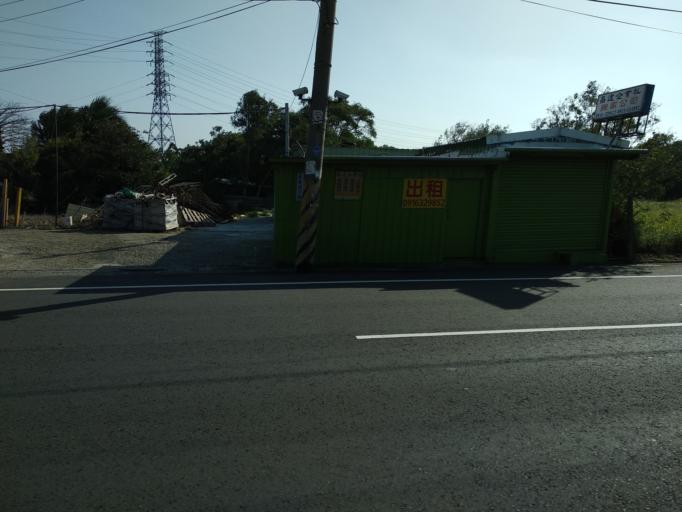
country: TW
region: Taiwan
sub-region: Hsinchu
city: Zhubei
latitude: 24.9882
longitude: 121.0368
